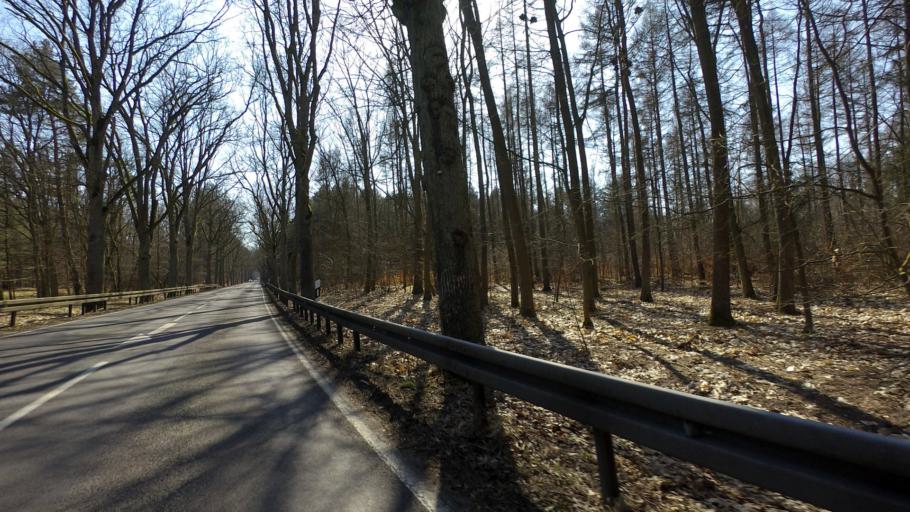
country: DE
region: Brandenburg
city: Leegebruch
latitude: 52.7767
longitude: 13.1607
